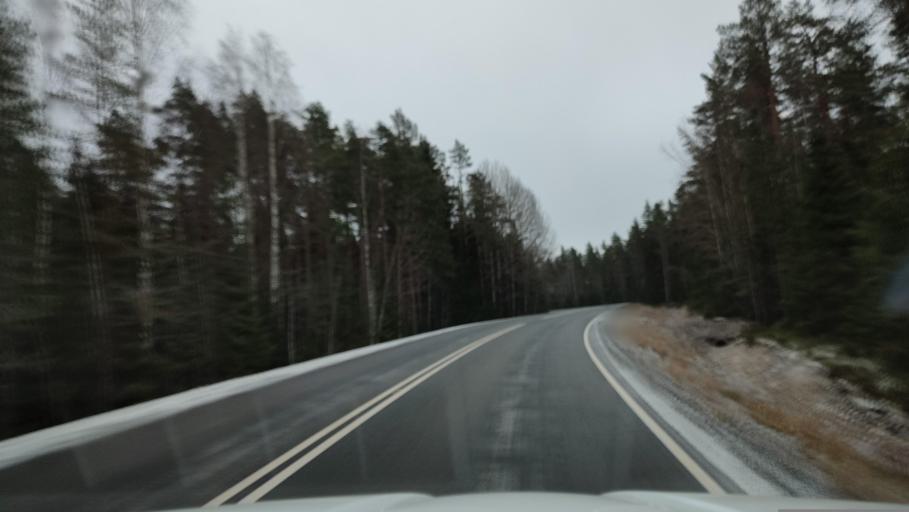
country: FI
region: Southern Ostrobothnia
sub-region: Suupohja
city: Karijoki
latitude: 62.2920
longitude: 21.6436
